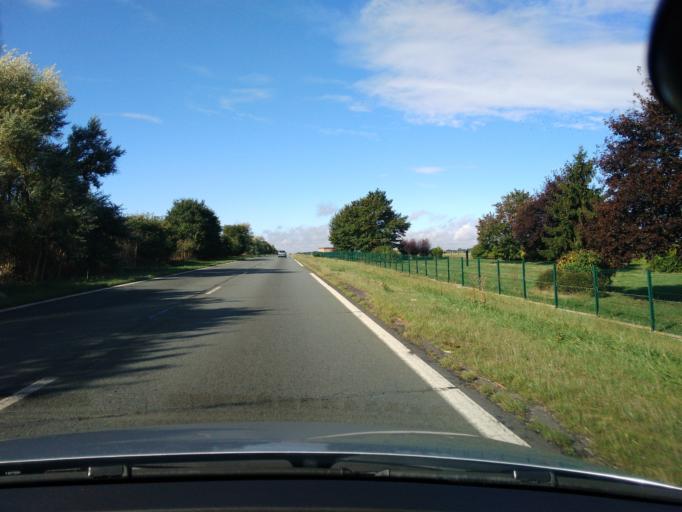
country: FR
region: Centre
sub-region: Departement d'Eure-et-Loir
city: Vert-en-Drouais
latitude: 48.7423
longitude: 1.3023
